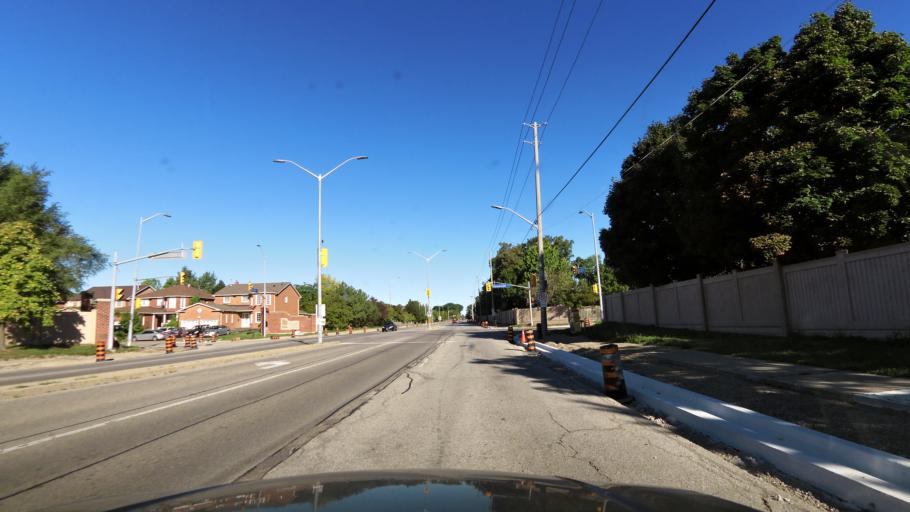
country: CA
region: Ontario
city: Mississauga
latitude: 43.5996
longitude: -79.6667
